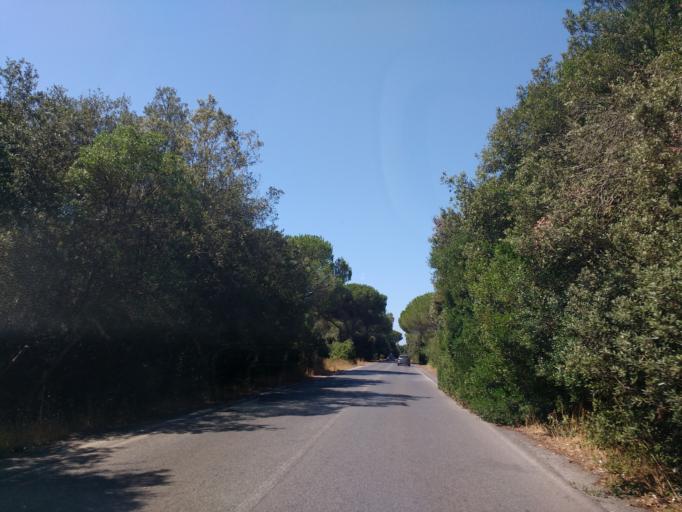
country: IT
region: Latium
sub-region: Citta metropolitana di Roma Capitale
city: Acilia-Castel Fusano-Ostia Antica
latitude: 41.7069
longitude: 12.3537
